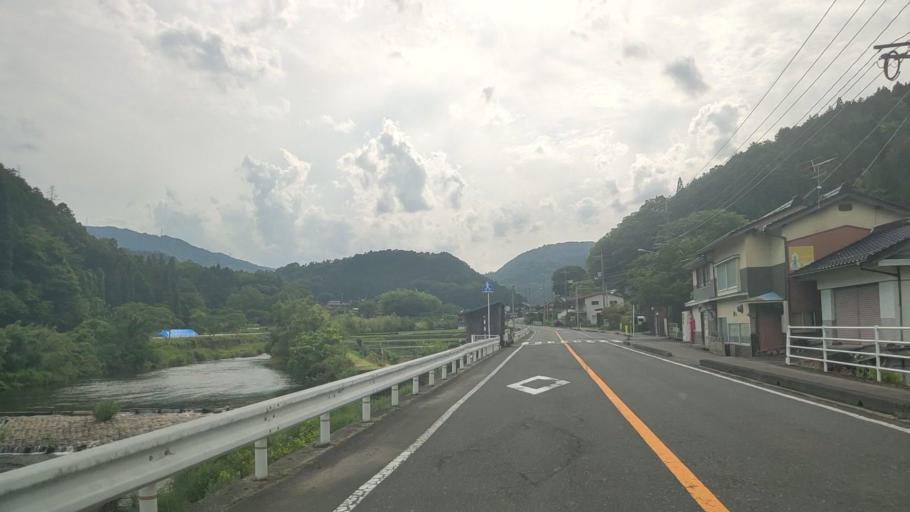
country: JP
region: Tottori
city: Tottori
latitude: 35.3421
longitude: 134.1752
